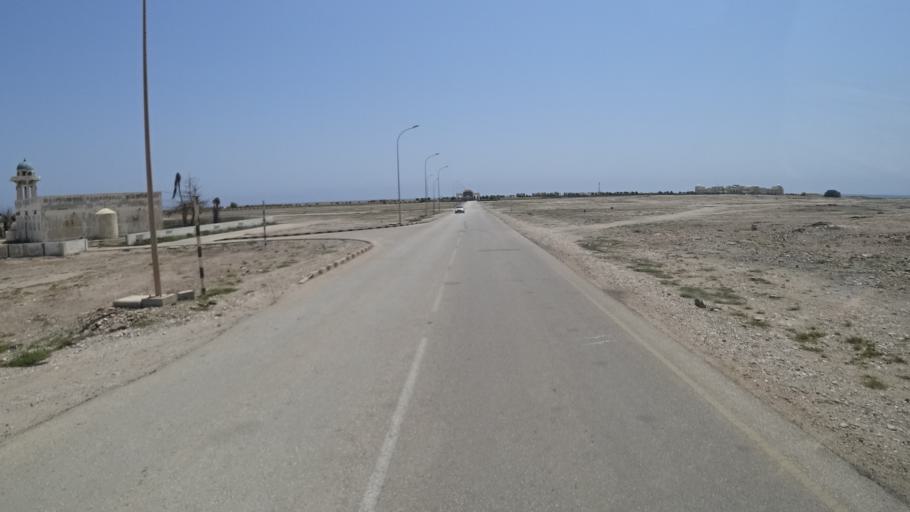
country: OM
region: Zufar
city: Salalah
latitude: 16.9650
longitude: 54.7384
